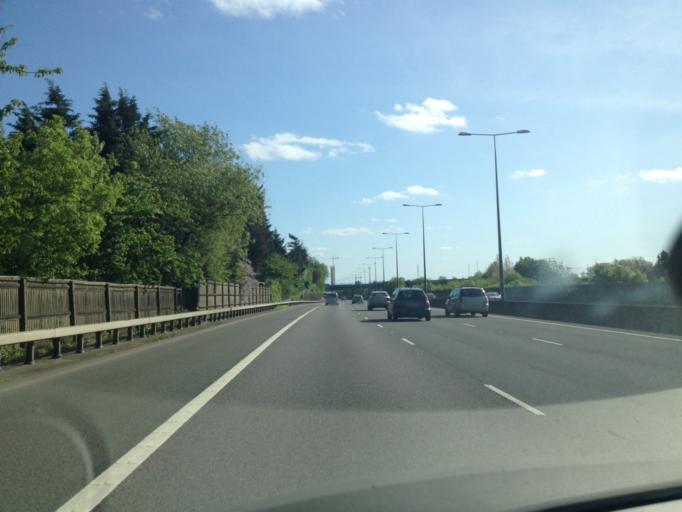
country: GB
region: England
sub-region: Greater London
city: Hendon
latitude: 51.5909
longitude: -0.2363
